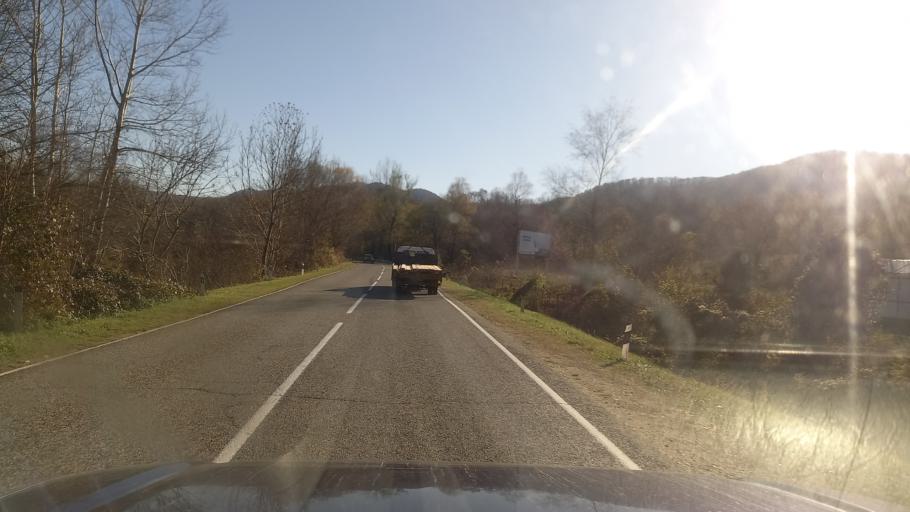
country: RU
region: Krasnodarskiy
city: Goryachiy Klyuch
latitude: 44.6000
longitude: 39.0820
